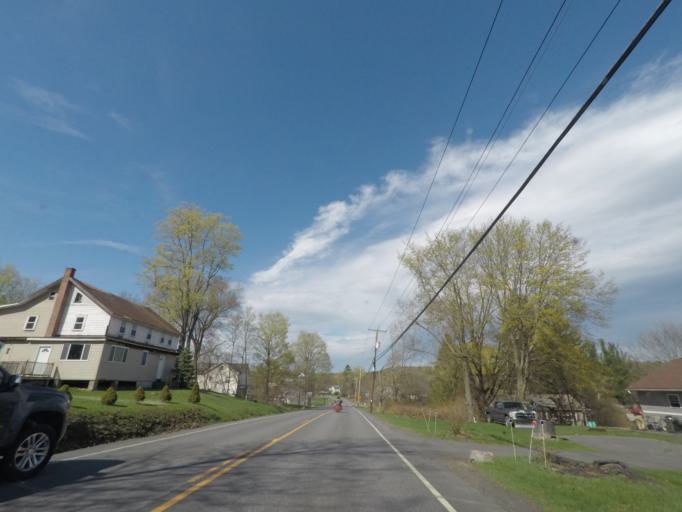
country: US
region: New York
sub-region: Greene County
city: Cairo
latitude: 42.4101
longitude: -74.0233
